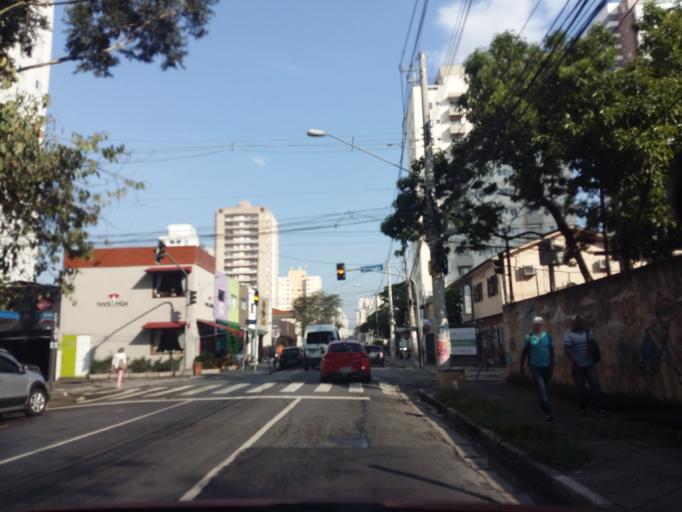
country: BR
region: Sao Paulo
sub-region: Sao Paulo
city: Sao Paulo
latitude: -23.6069
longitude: -46.6910
